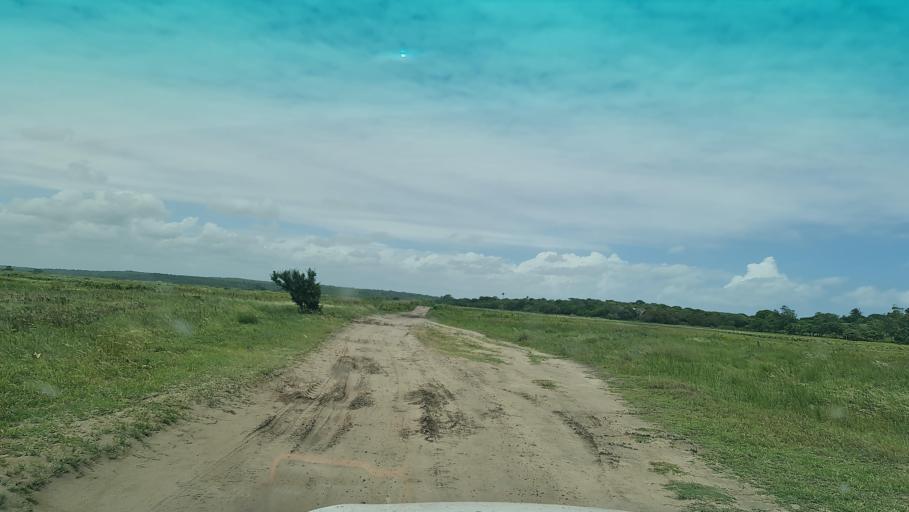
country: MZ
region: Maputo
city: Manhica
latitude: -25.5256
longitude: 32.8556
